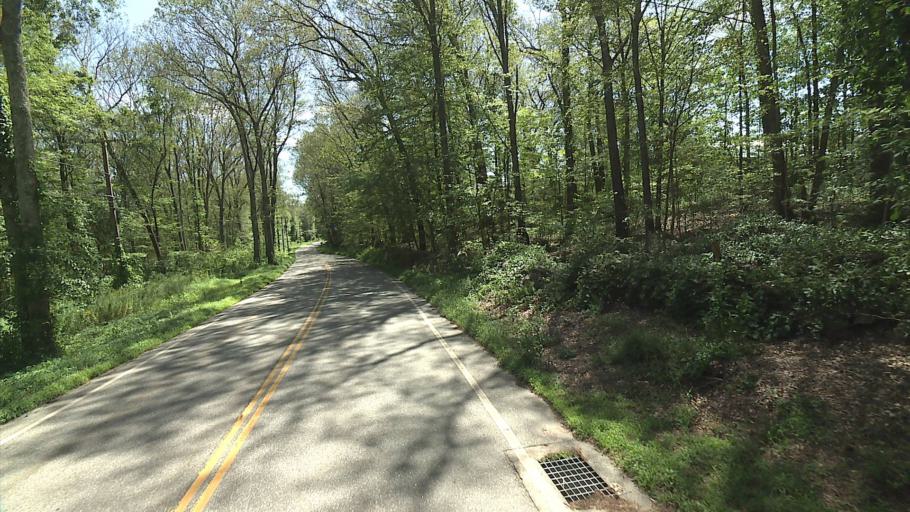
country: US
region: Connecticut
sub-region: Windham County
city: Windham
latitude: 41.7353
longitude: -72.0672
